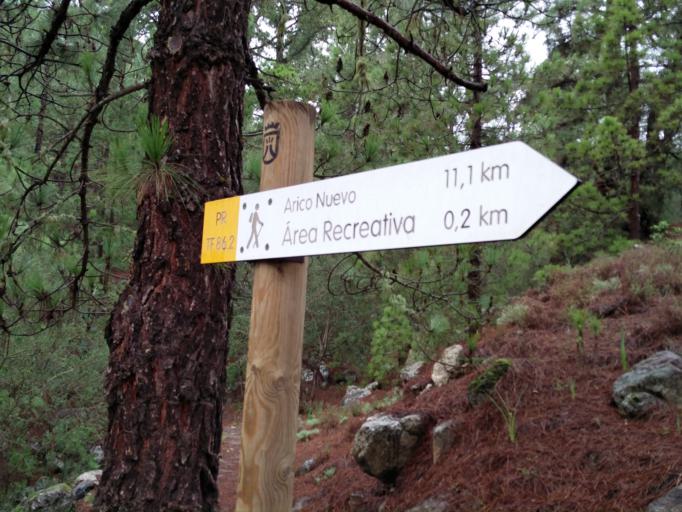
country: ES
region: Canary Islands
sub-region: Provincia de Santa Cruz de Tenerife
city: Lomo de Arico
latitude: 28.2060
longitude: -16.5387
